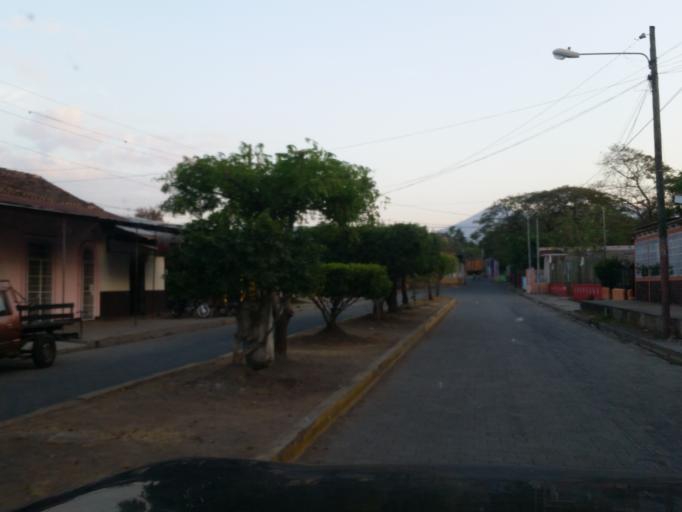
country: NI
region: Granada
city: Granada
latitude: 11.9385
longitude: -85.9544
